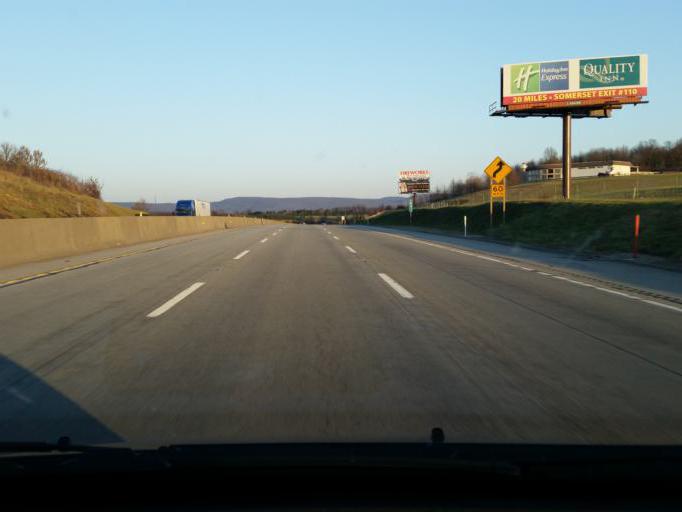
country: US
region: Pennsylvania
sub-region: Fayette County
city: Bear Rocks
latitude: 40.1246
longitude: -79.4024
